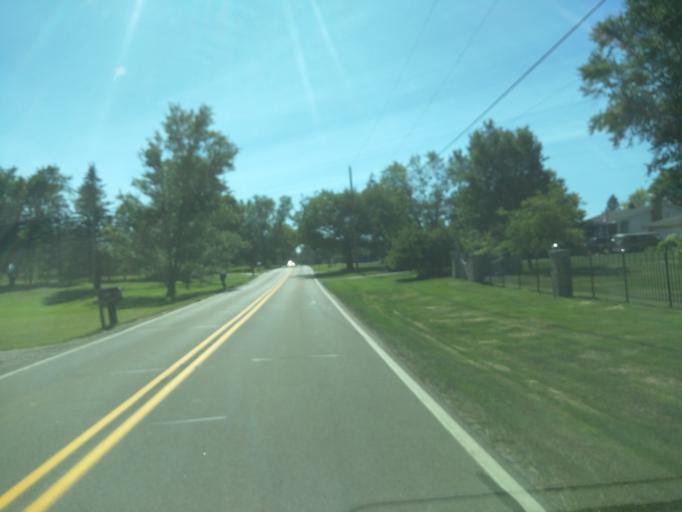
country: US
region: Michigan
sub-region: Eaton County
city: Waverly
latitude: 42.7649
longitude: -84.6425
